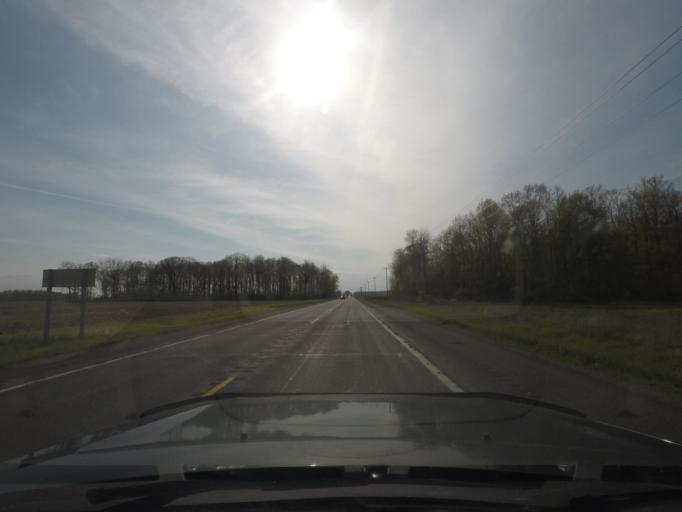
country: US
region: Michigan
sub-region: Berrien County
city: Three Oaks
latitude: 41.7982
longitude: -86.5353
